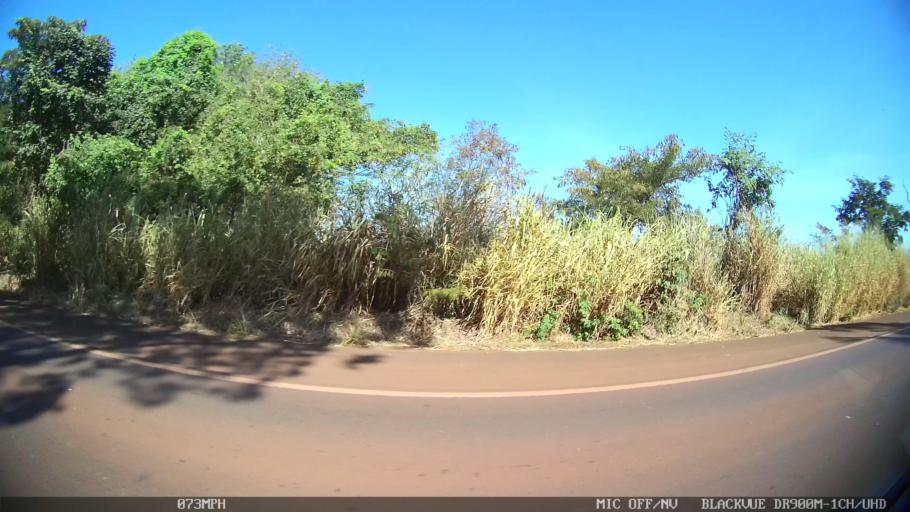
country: BR
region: Sao Paulo
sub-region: Guaira
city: Guaira
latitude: -20.4435
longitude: -48.3240
